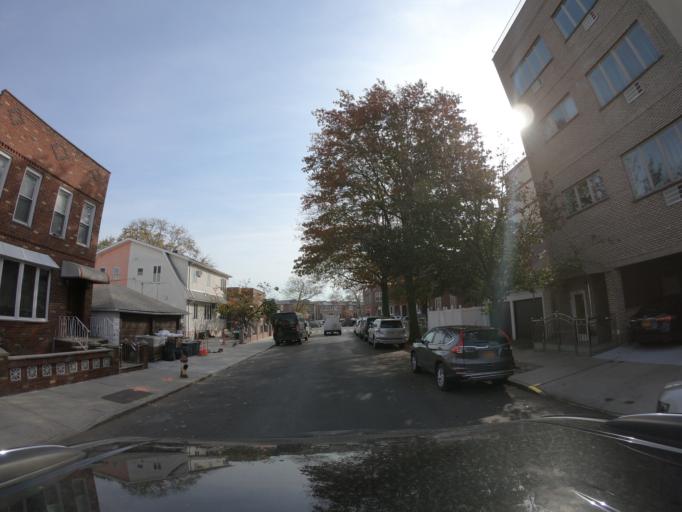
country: US
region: New York
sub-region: Kings County
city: Bensonhurst
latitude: 40.6132
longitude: -73.9757
